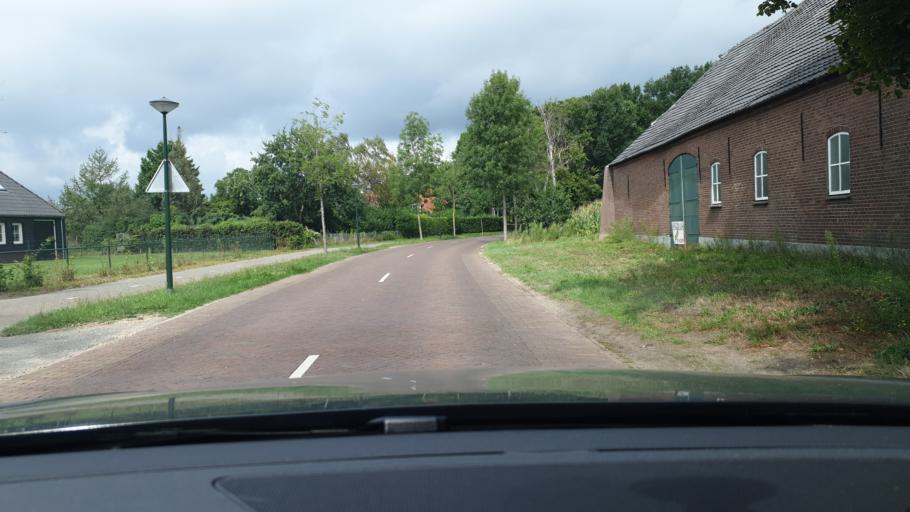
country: NL
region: North Brabant
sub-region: Gemeente Son en Breugel
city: Breugel
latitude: 51.5000
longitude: 5.5121
